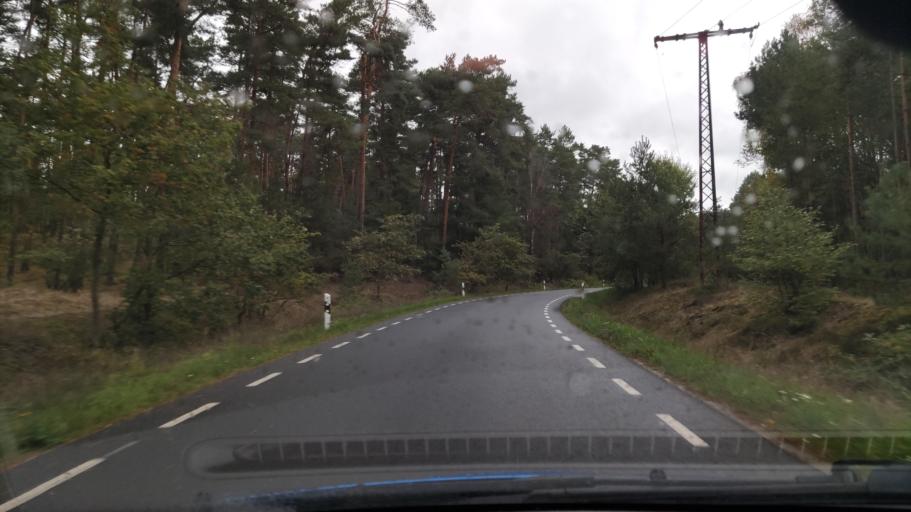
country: DE
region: Lower Saxony
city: Gartow
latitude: 52.9806
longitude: 11.5441
